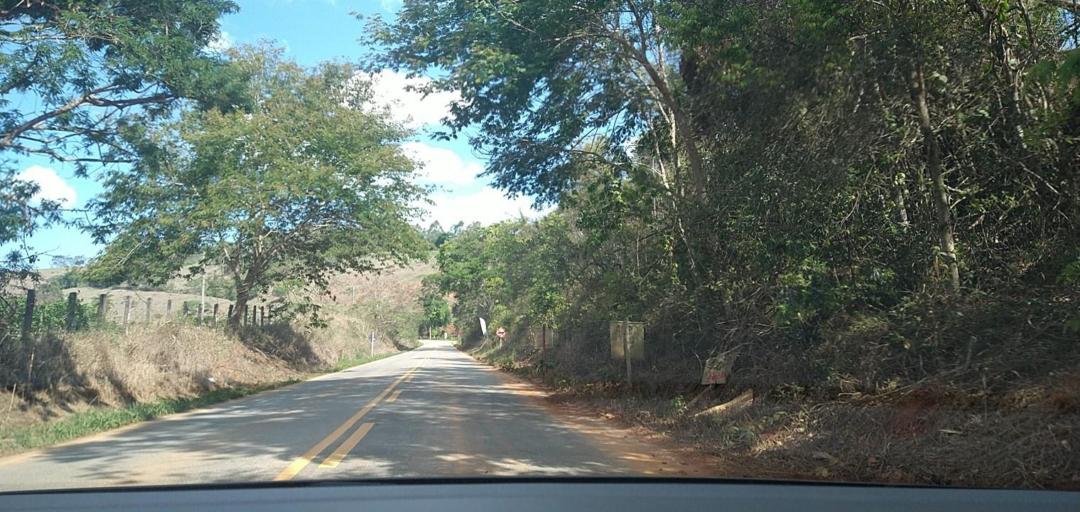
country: BR
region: Minas Gerais
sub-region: Alvinopolis
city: Alvinopolis
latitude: -20.0152
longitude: -43.0952
